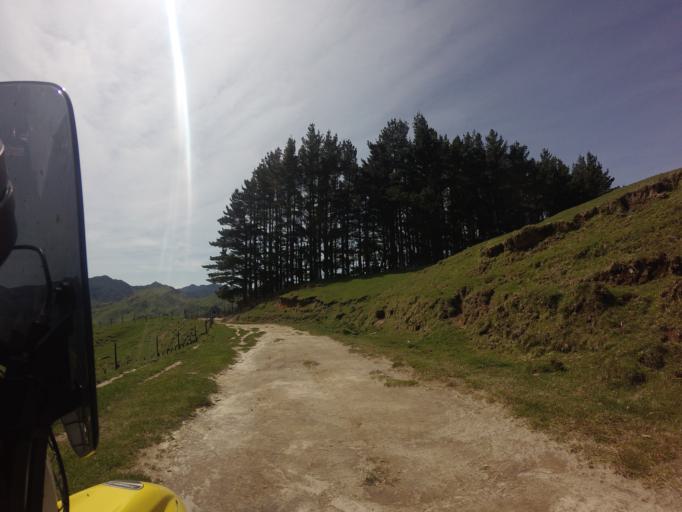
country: NZ
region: Bay of Plenty
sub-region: Opotiki District
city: Opotiki
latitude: -38.4709
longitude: 177.3791
